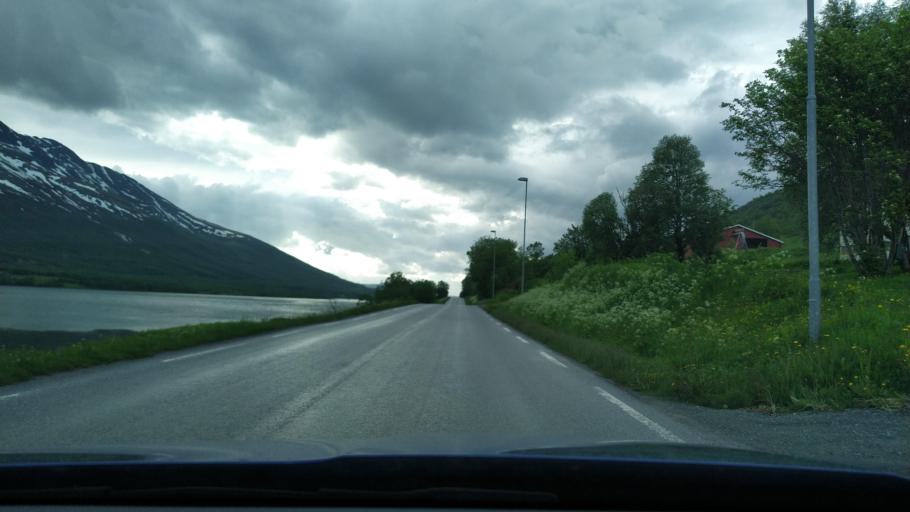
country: NO
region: Troms
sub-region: Balsfjord
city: Storsteinnes
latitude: 69.2204
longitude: 19.5349
